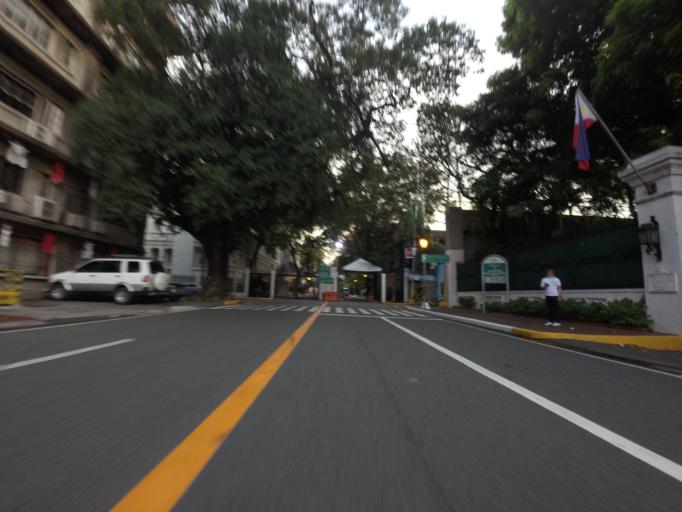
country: PH
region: Metro Manila
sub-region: City of Manila
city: Quiapo
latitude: 14.5922
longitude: 120.9895
